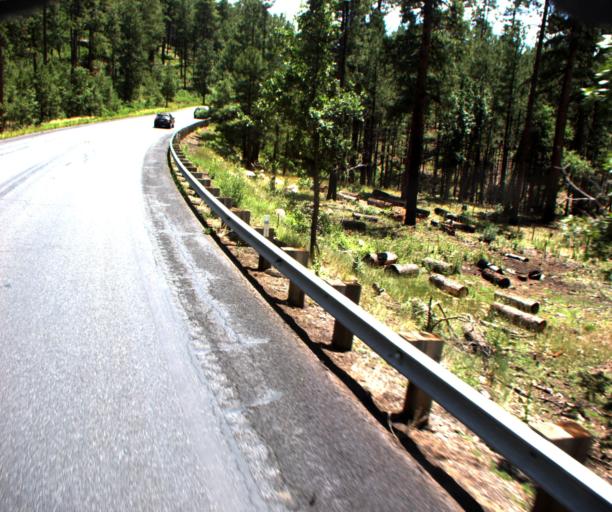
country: US
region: Arizona
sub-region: Gila County
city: Pine
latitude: 34.4646
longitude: -111.4436
